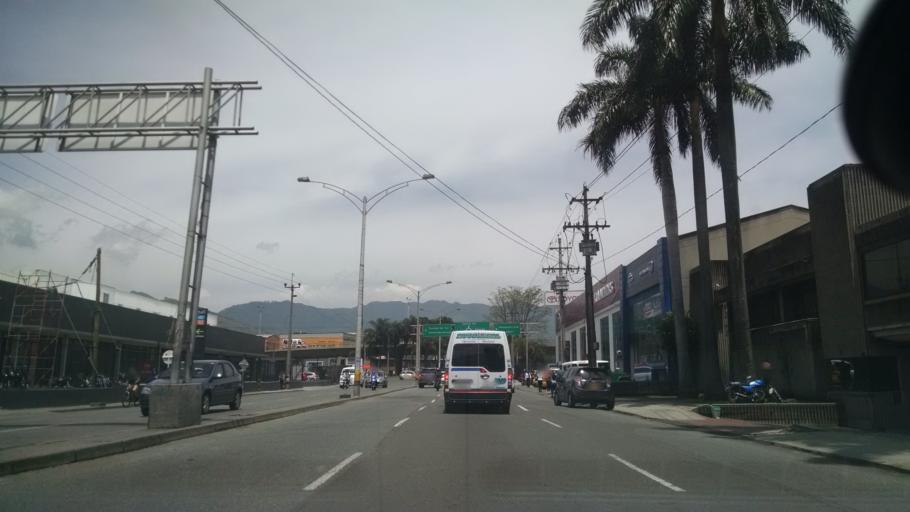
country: CO
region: Antioquia
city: Itagui
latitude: 6.2143
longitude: -75.5802
